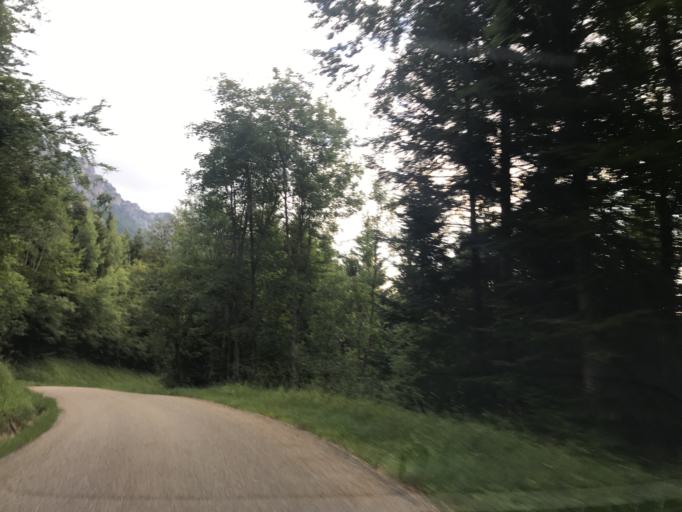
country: FR
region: Rhone-Alpes
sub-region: Departement de l'Isere
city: Le Touvet
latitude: 45.3639
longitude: 5.9206
